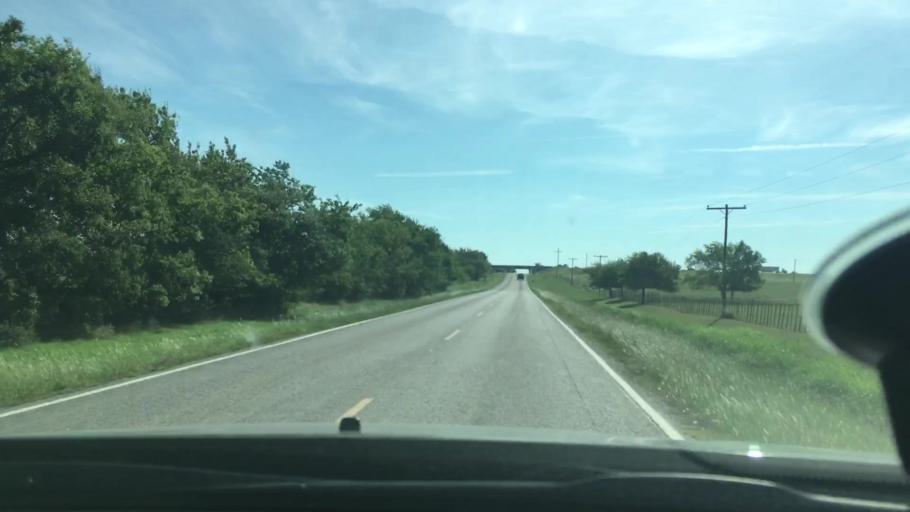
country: US
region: Oklahoma
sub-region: Carter County
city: Ardmore
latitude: 34.3327
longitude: -97.1599
